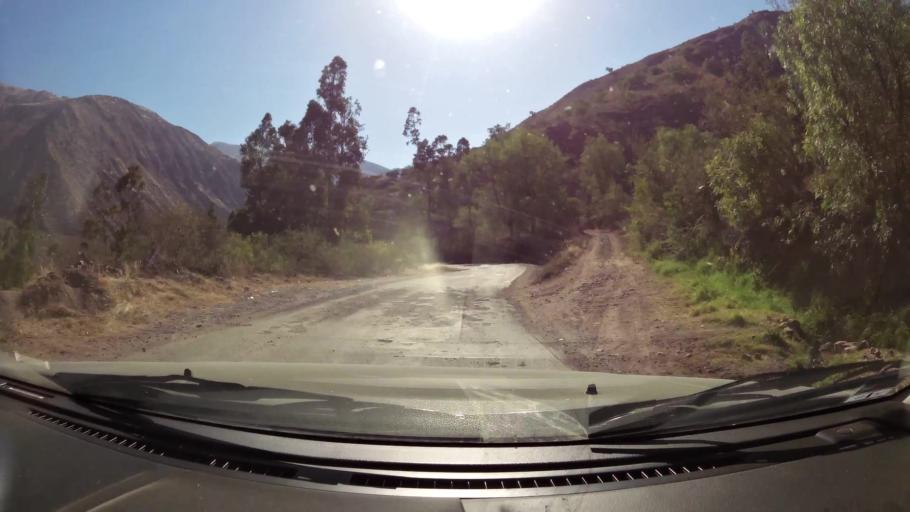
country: PE
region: Huancavelica
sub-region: Provincia de Acobamba
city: Pomacocha
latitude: -12.7631
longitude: -74.5159
